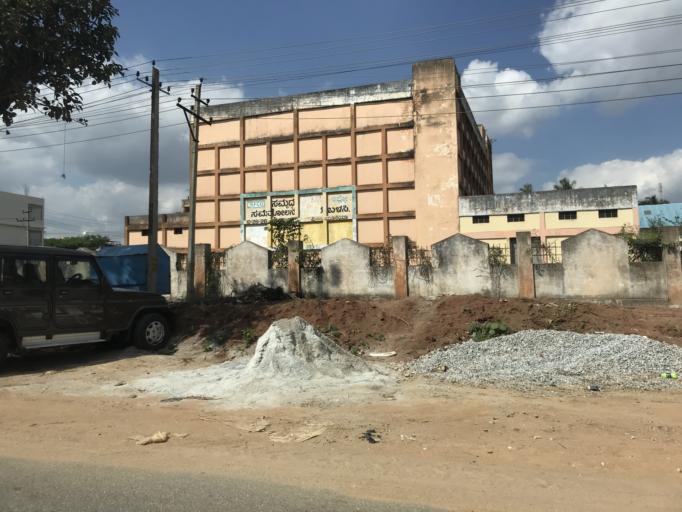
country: IN
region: Karnataka
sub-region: Hassan
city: Hassan
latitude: 12.9942
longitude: 76.0747
